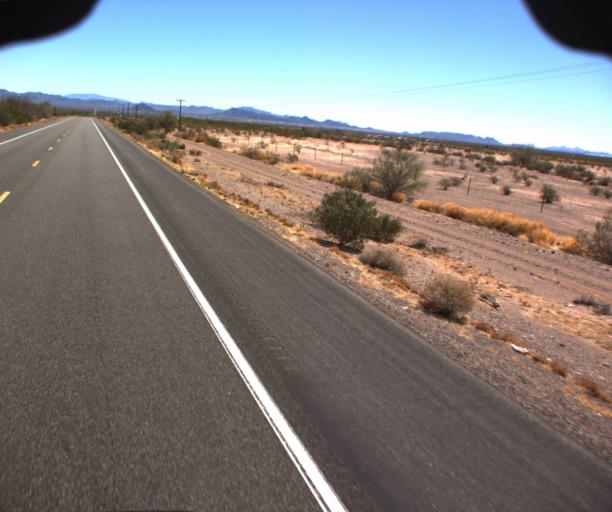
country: US
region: Arizona
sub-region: La Paz County
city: Salome
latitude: 33.6952
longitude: -113.8795
